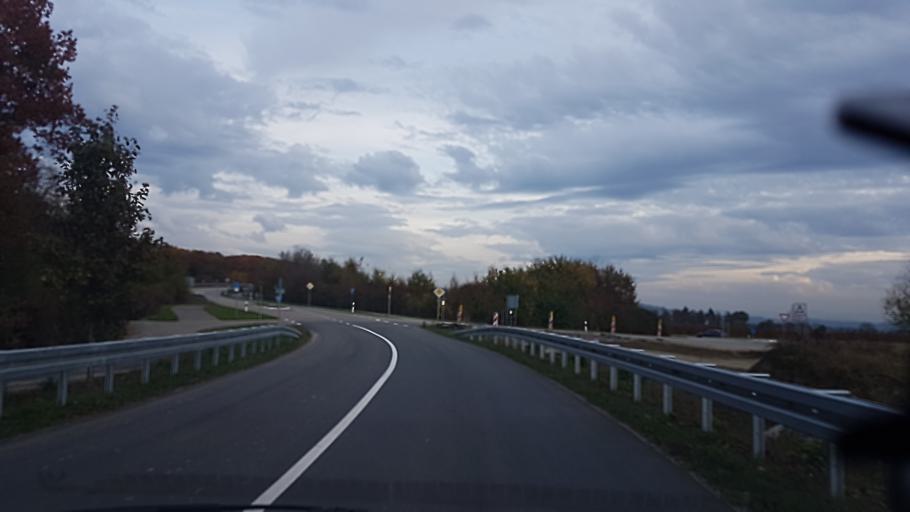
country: DE
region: Baden-Wuerttemberg
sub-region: Freiburg Region
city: Rust
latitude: 48.2600
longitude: 7.7455
